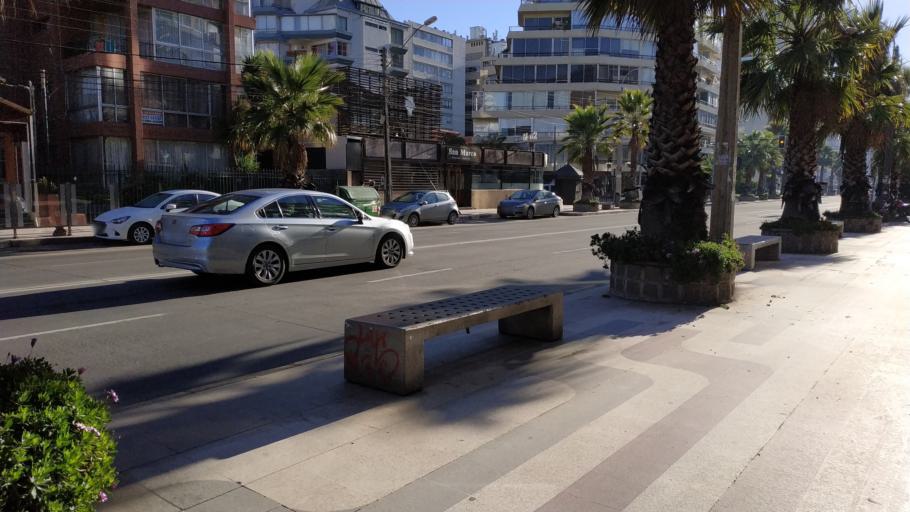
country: CL
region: Valparaiso
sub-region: Provincia de Valparaiso
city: Vina del Mar
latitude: -33.0159
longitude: -71.5565
